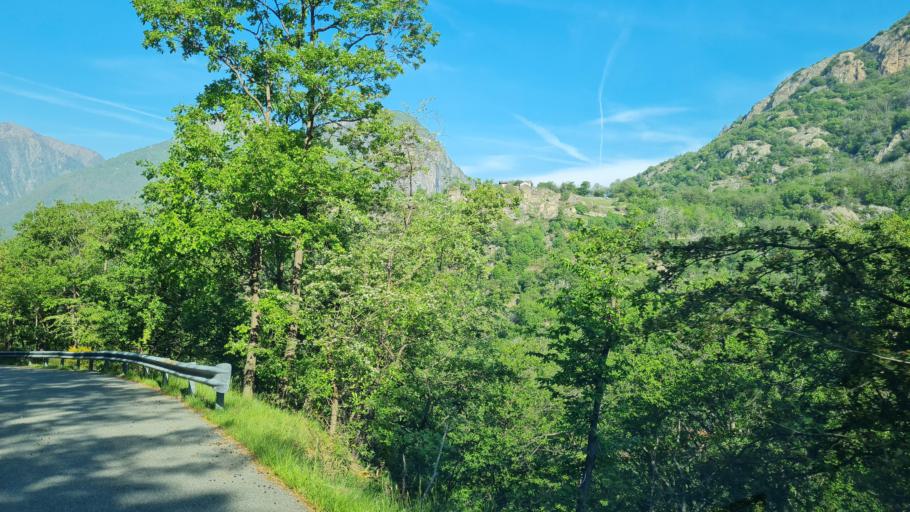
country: IT
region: Aosta Valley
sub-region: Valle d'Aosta
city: Bard
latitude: 45.6126
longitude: 7.7555
